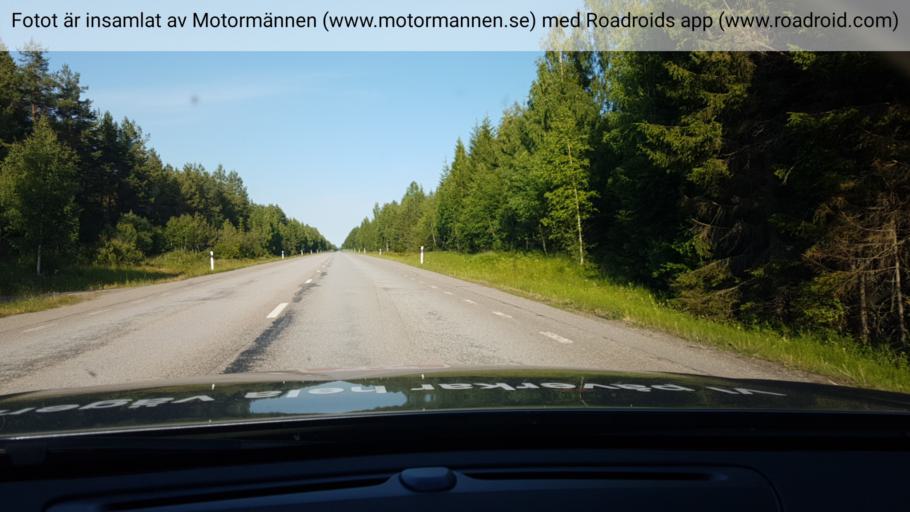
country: SE
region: Uppsala
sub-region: Osthammars Kommun
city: Gimo
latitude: 60.1639
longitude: 18.0926
